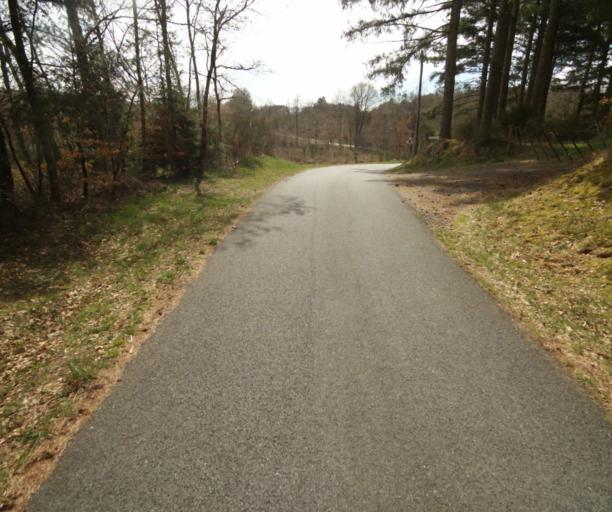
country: FR
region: Limousin
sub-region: Departement de la Correze
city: Egletons
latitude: 45.3700
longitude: 1.9690
